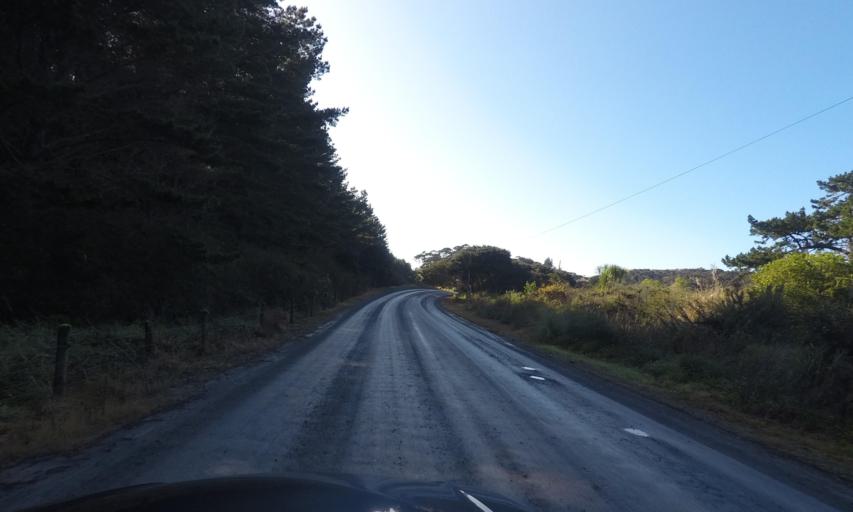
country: NZ
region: Auckland
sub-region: Auckland
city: Wellsford
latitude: -36.1611
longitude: 174.6369
